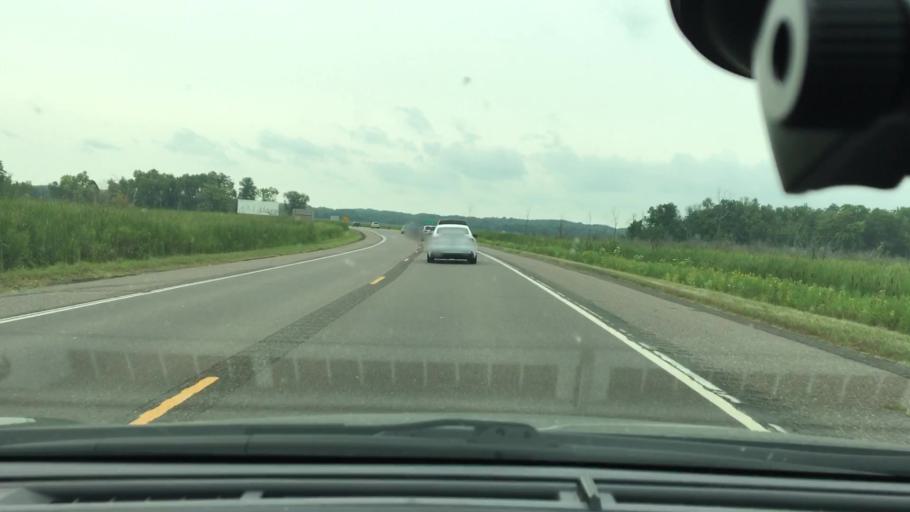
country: US
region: Minnesota
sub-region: Mille Lacs County
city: Vineland
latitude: 46.1663
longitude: -93.7597
